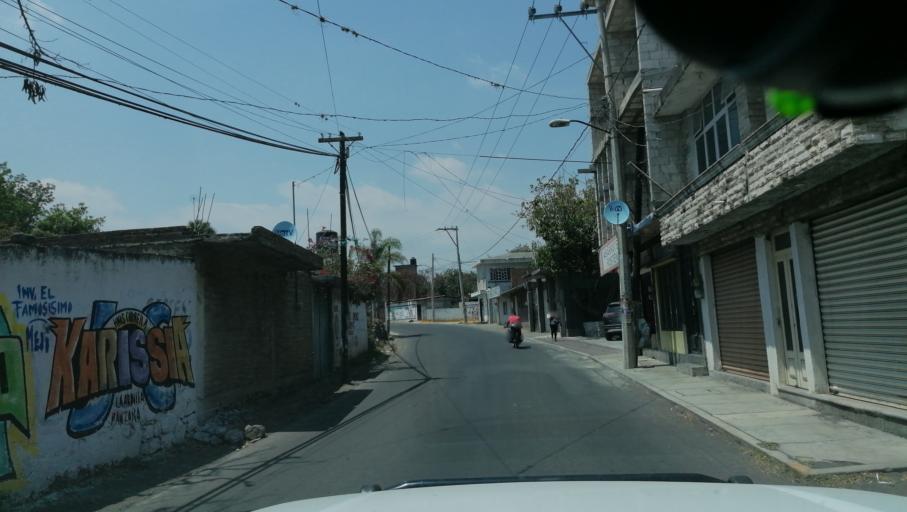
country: MX
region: Puebla
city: Atlixco
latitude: 18.9107
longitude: -98.4703
